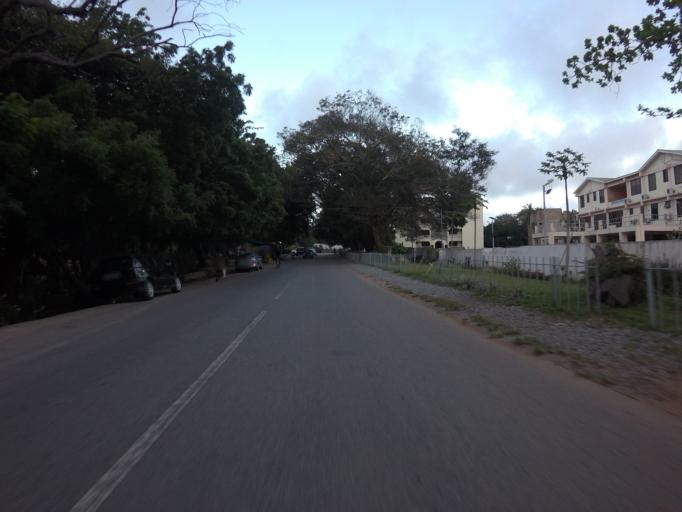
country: GH
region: Greater Accra
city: Accra
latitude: 5.5722
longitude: -0.1855
